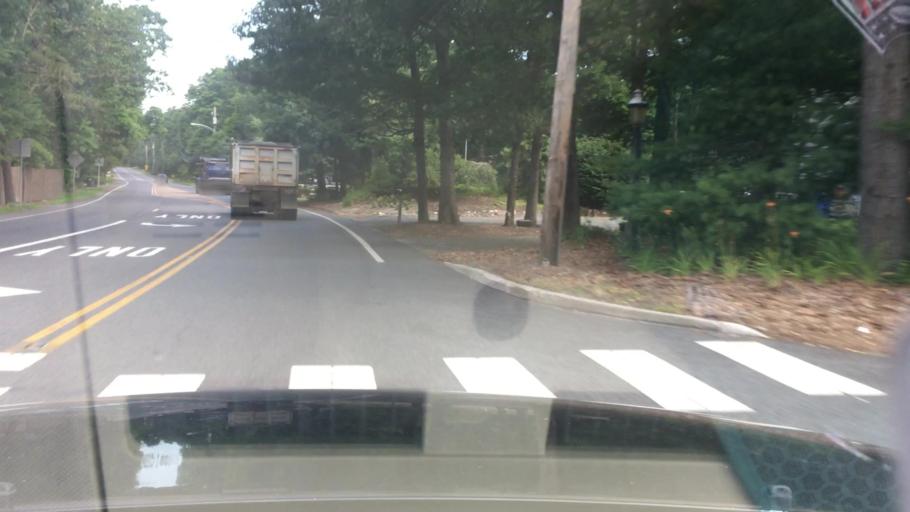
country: US
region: New Jersey
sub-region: Ocean County
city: Vista Center
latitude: 40.1502
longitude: -74.3988
